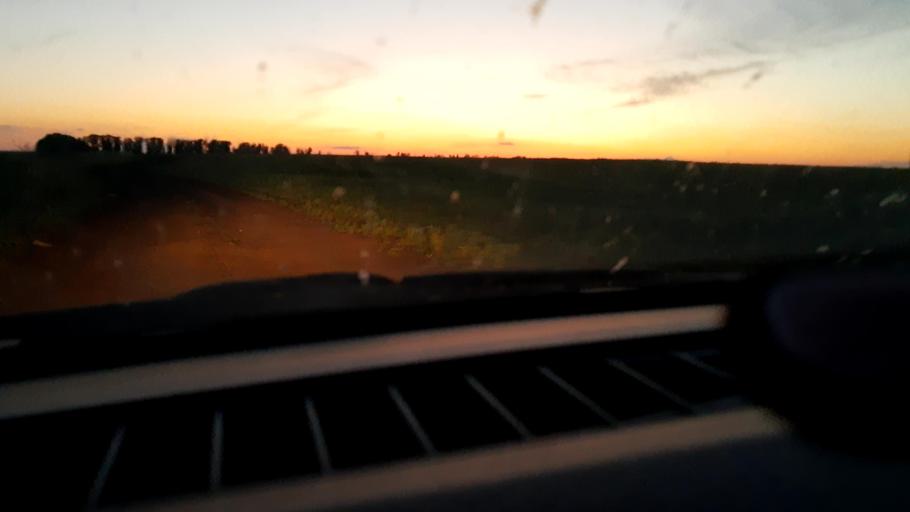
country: RU
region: Bashkortostan
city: Asanovo
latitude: 54.8615
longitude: 55.5878
